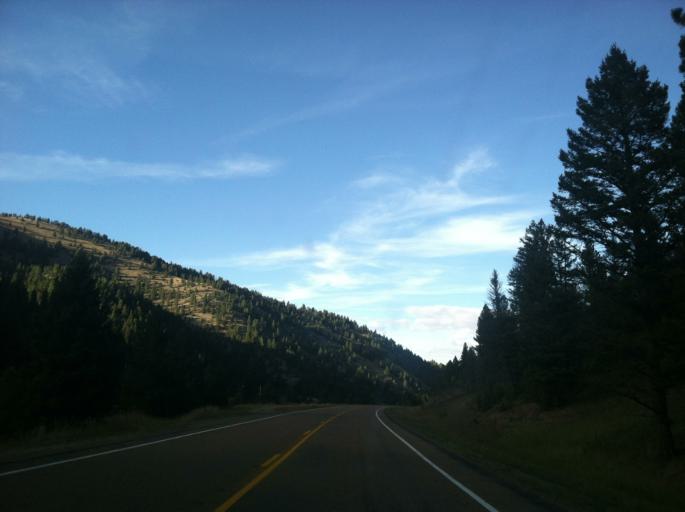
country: US
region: Montana
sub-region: Granite County
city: Philipsburg
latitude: 46.4269
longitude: -113.2745
